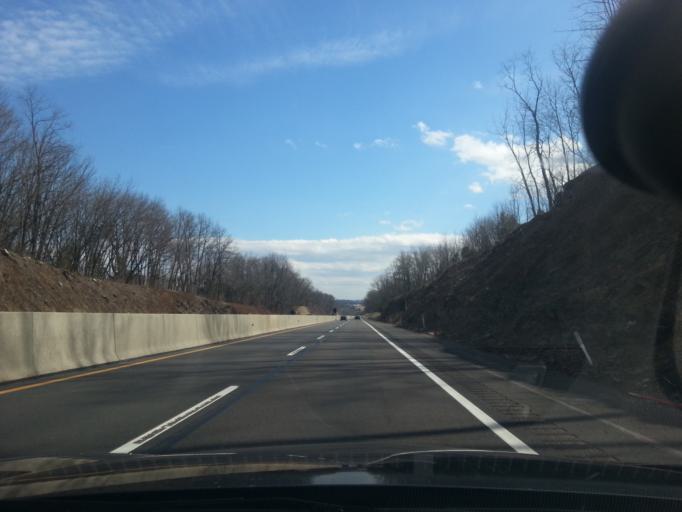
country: US
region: Pennsylvania
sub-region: Montgomery County
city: Telford
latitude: 40.3460
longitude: -75.3883
